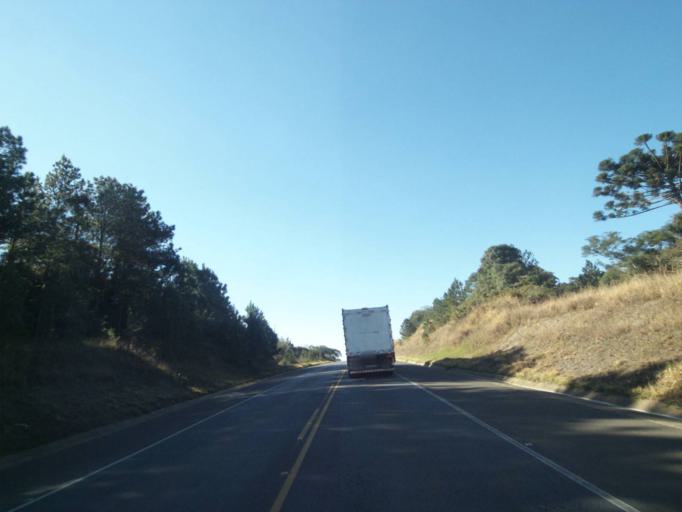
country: BR
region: Parana
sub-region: Tibagi
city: Tibagi
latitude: -24.5449
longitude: -50.4500
